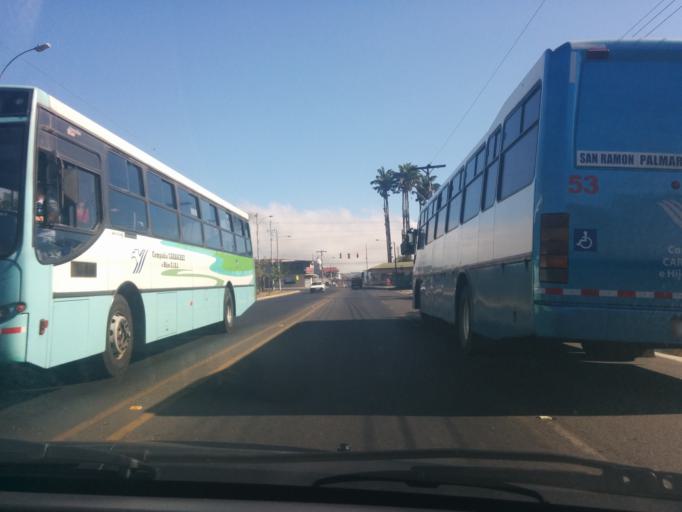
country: CR
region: Alajuela
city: San Ramon
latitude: 10.0811
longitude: -84.4696
